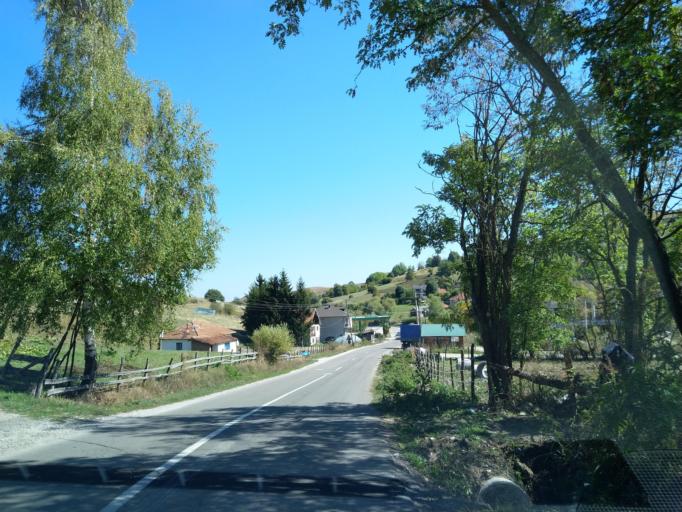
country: RS
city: Sokolovica
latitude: 43.2490
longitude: 20.2310
